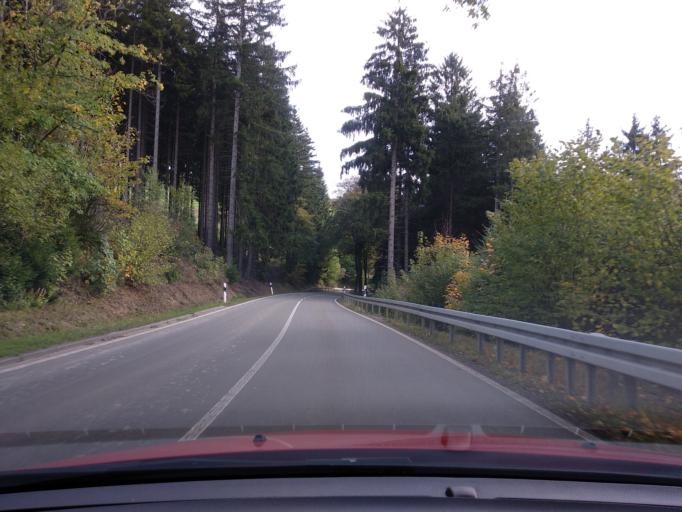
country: DE
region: North Rhine-Westphalia
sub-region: Regierungsbezirk Arnsberg
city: Bestwig
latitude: 51.3259
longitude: 8.4055
